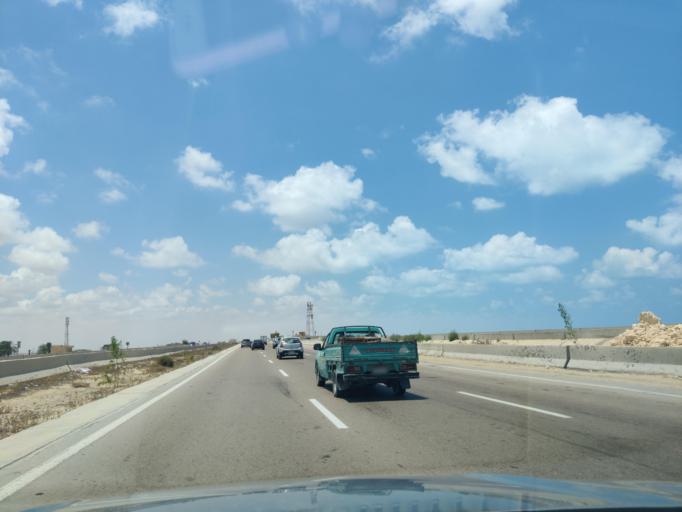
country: EG
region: Muhafazat Matruh
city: Al `Alamayn
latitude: 30.8277
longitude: 29.2041
